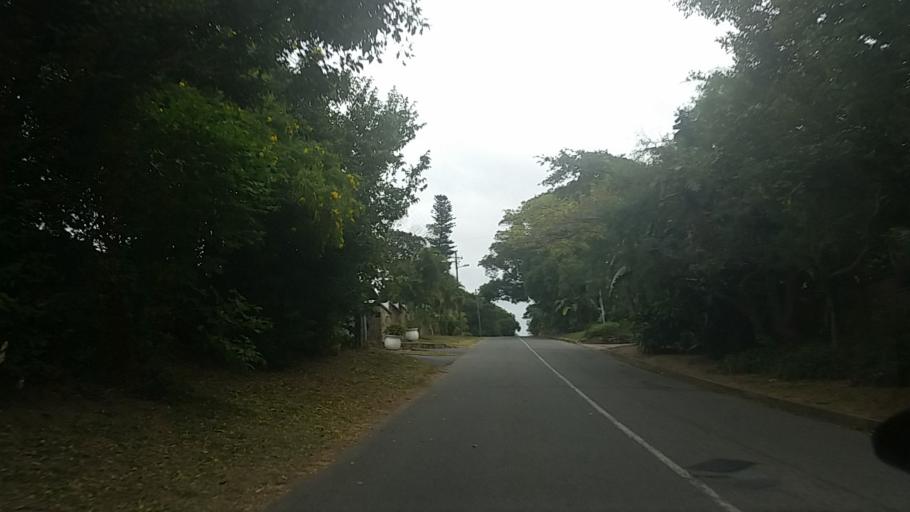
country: ZA
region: KwaZulu-Natal
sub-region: eThekwini Metropolitan Municipality
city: Berea
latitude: -29.8384
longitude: 30.9359
